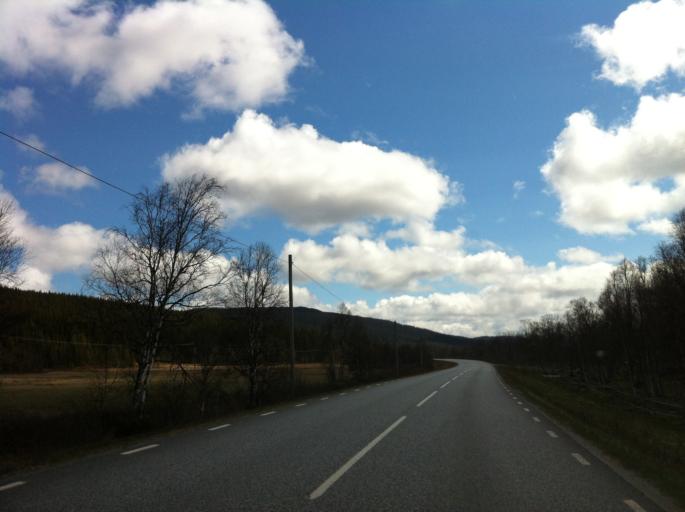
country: NO
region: Sor-Trondelag
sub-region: Tydal
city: Aas
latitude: 62.6048
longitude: 12.5100
